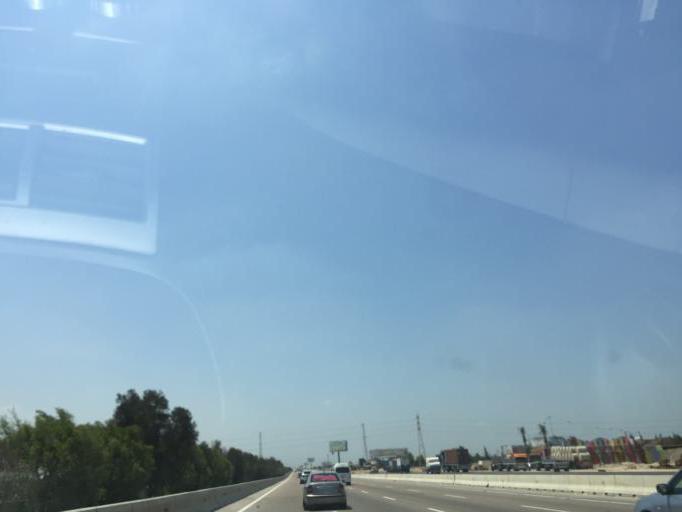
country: EG
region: Al Buhayrah
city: Beheira
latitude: 30.4150
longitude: 30.3549
